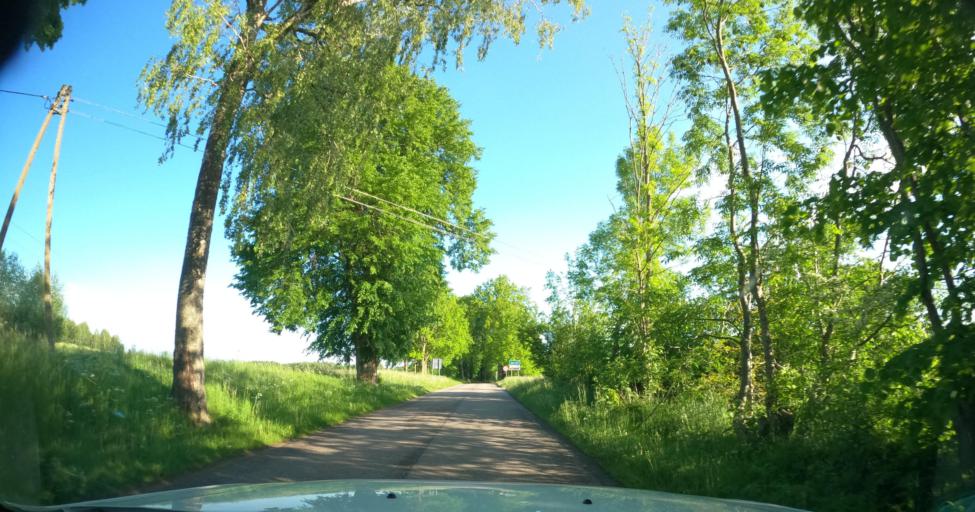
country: PL
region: Warmian-Masurian Voivodeship
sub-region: Powiat braniewski
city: Pieniezno
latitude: 54.2425
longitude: 20.0284
